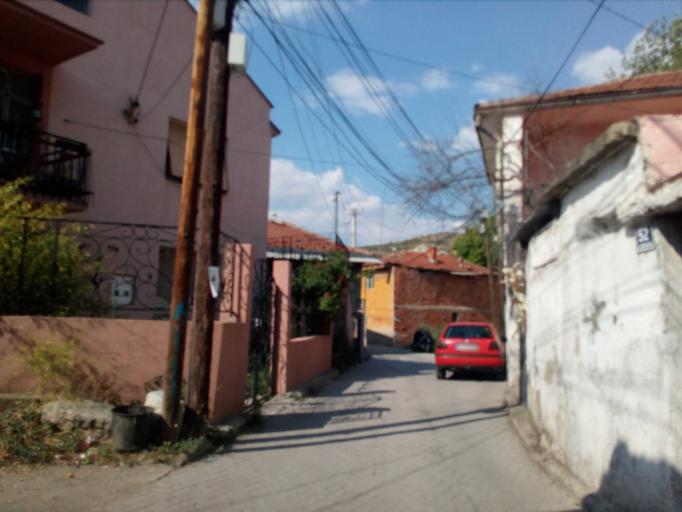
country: MK
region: Veles
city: Veles
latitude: 41.7181
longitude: 21.7848
